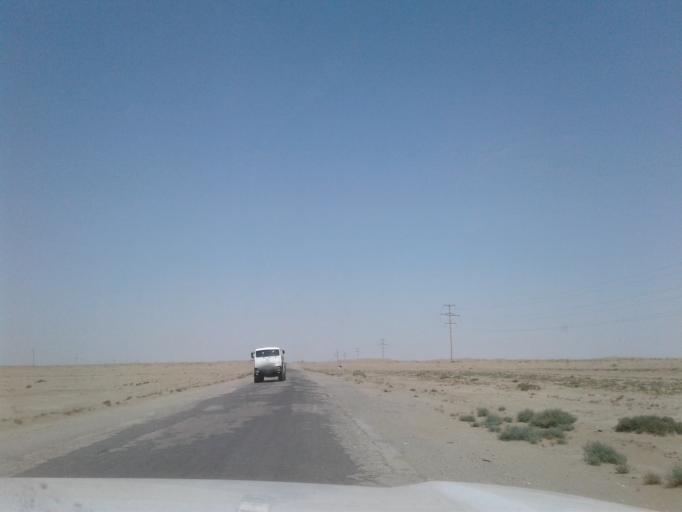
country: TM
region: Balkan
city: Gumdag
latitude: 38.3628
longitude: 54.3822
